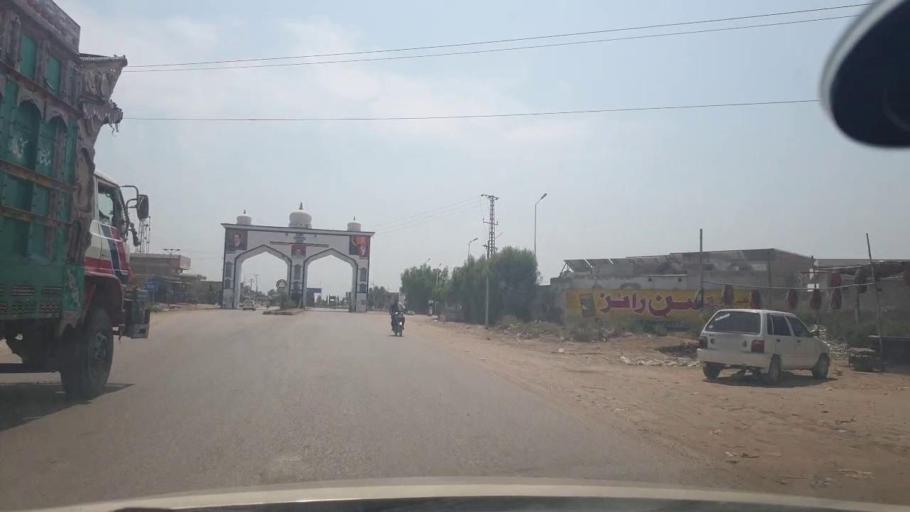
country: PK
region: Sindh
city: Jacobabad
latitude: 28.2432
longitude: 68.4681
